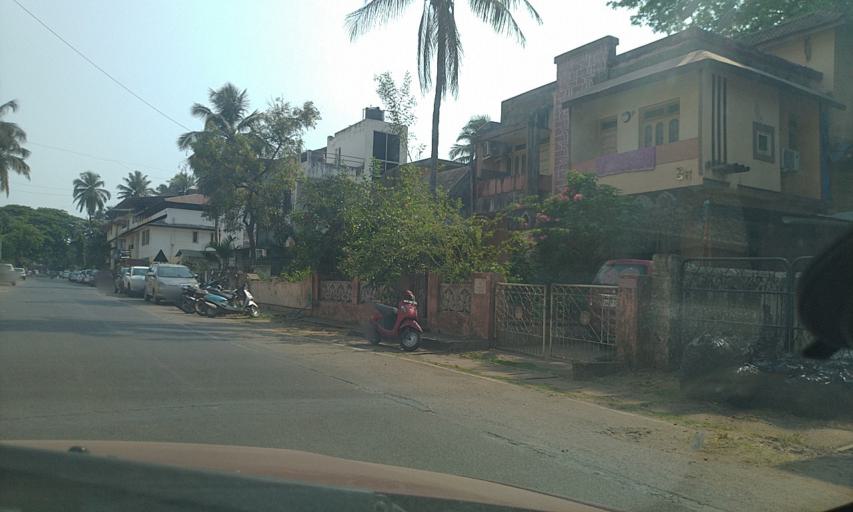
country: IN
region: Goa
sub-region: North Goa
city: Panaji
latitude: 15.4869
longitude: 73.8135
